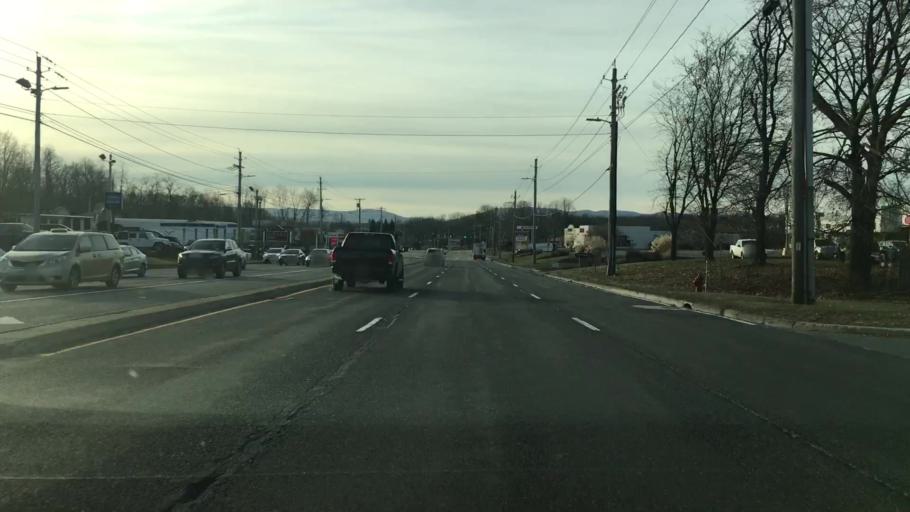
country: US
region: New York
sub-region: Dutchess County
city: Crown Heights
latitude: 41.6239
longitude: -73.9177
